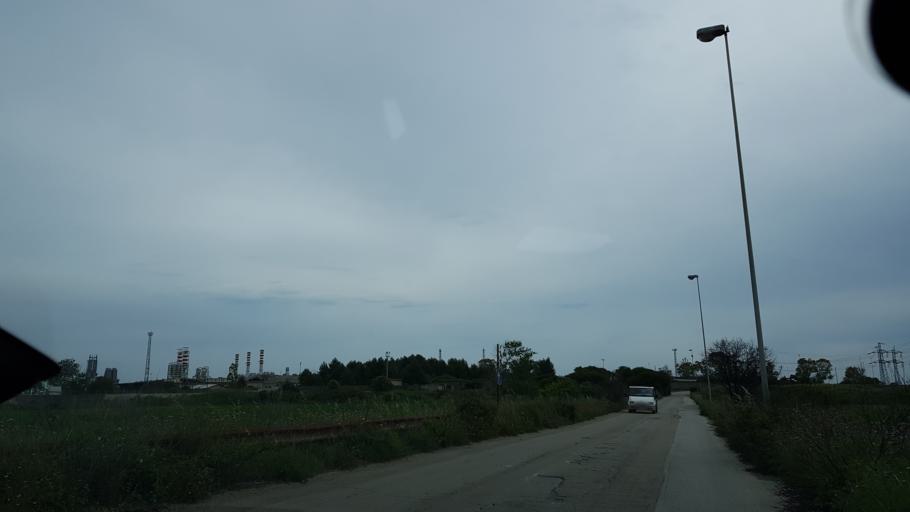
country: IT
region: Apulia
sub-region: Provincia di Brindisi
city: La Rosa
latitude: 40.6261
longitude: 17.9853
